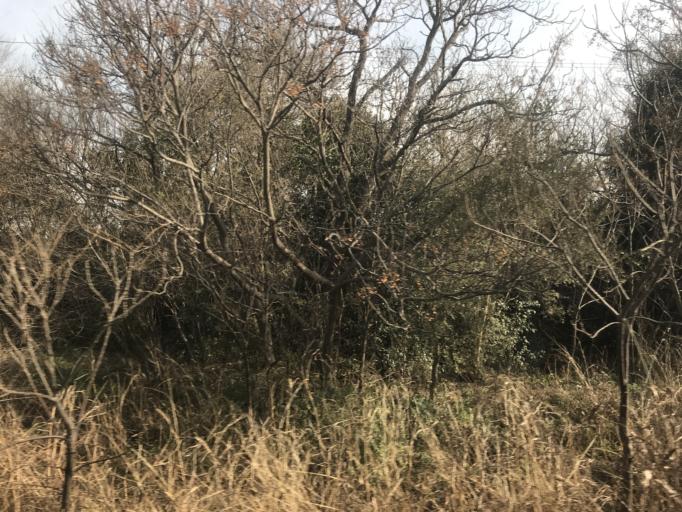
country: AR
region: Cordoba
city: Laguna Larga
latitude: -31.7852
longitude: -63.7960
